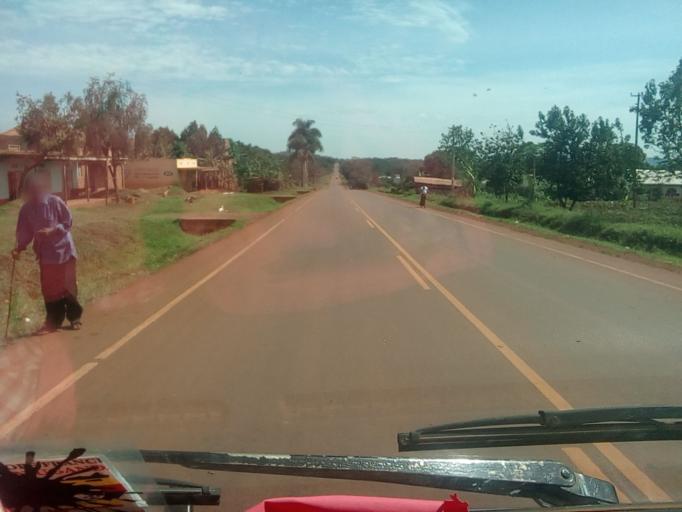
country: UG
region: Eastern Region
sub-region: Jinja District
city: Bugembe
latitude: 0.4927
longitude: 33.2236
